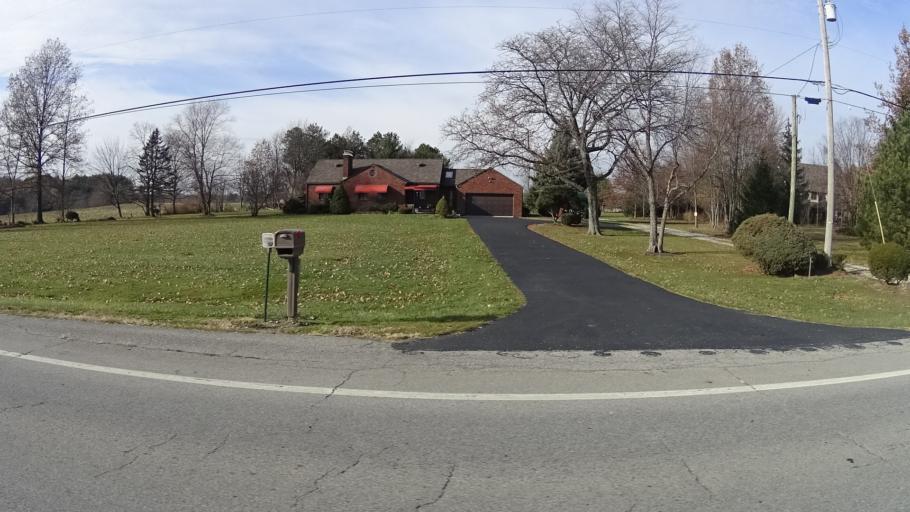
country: US
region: Ohio
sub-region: Lorain County
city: Grafton
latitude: 41.2107
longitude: -82.0237
